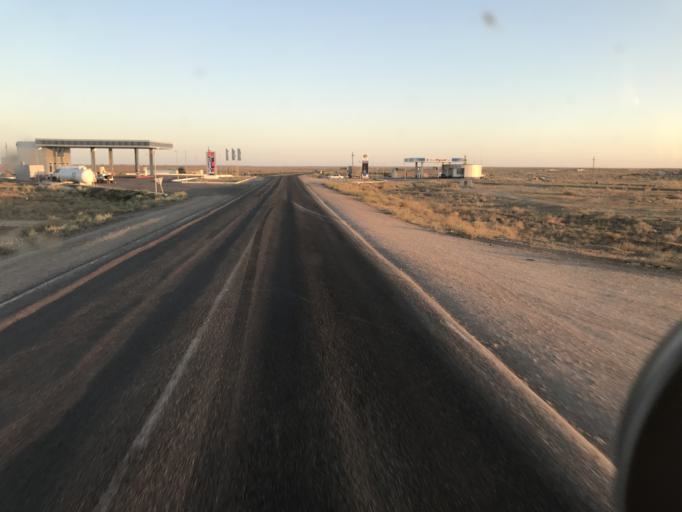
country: KZ
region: Qaraghandy
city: Saryshaghan
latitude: 46.0210
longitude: 73.5915
